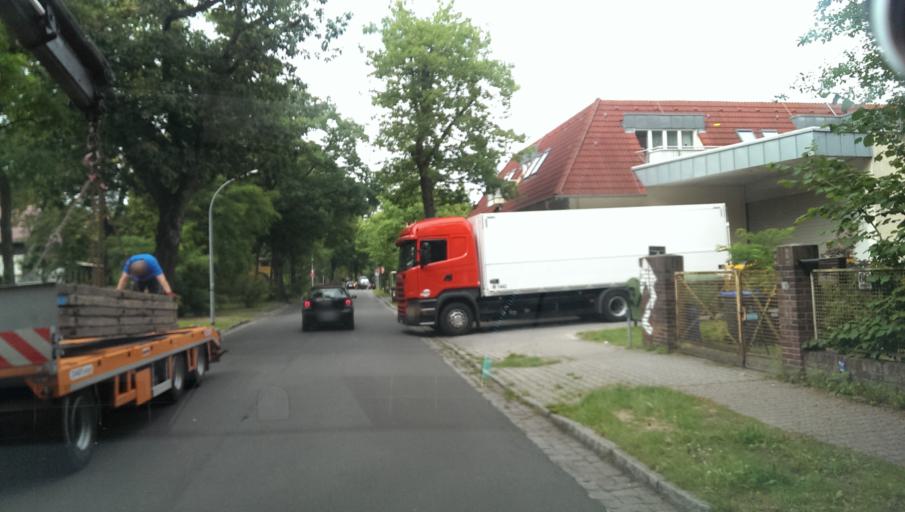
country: DE
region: Brandenburg
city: Kleinmachnow
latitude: 52.4128
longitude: 13.2237
